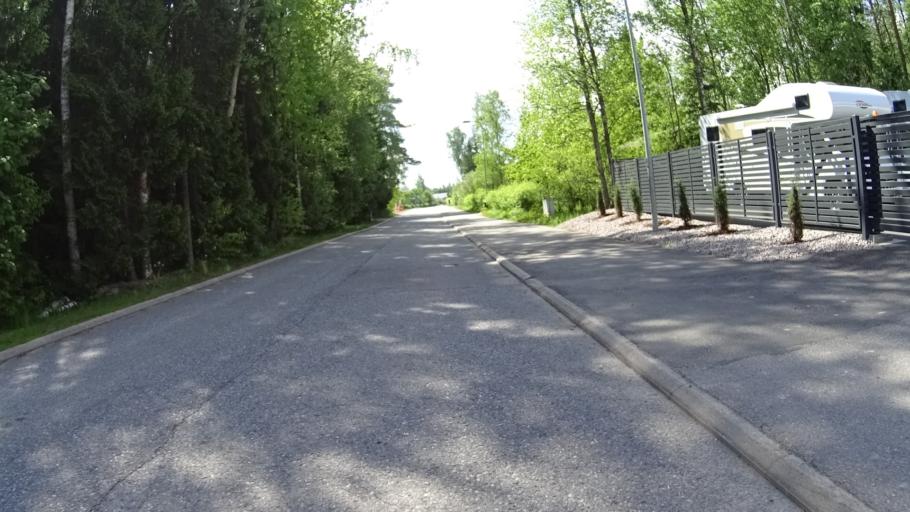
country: FI
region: Uusimaa
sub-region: Helsinki
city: Espoo
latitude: 60.2252
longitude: 24.6405
